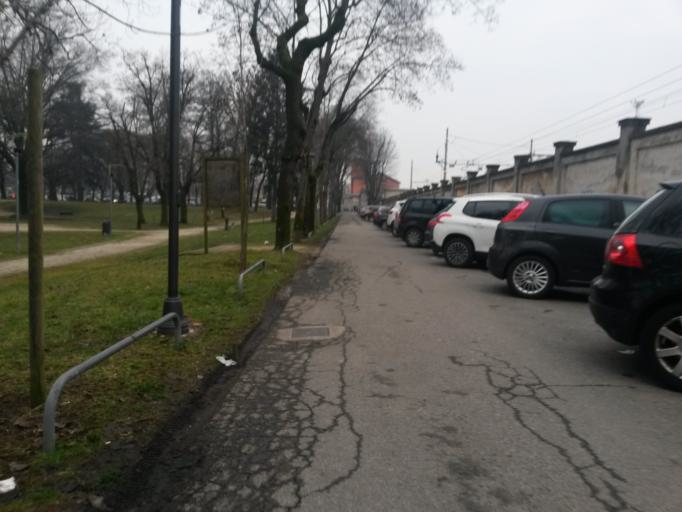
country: IT
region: Piedmont
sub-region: Provincia di Vercelli
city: Vercelli
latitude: 45.3306
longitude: 8.4189
